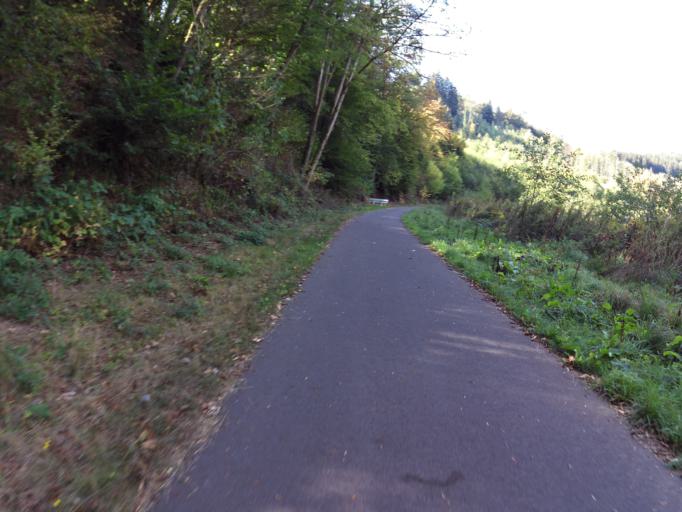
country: DE
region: Rheinland-Pfalz
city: Scheuern
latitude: 50.0028
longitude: 6.3089
